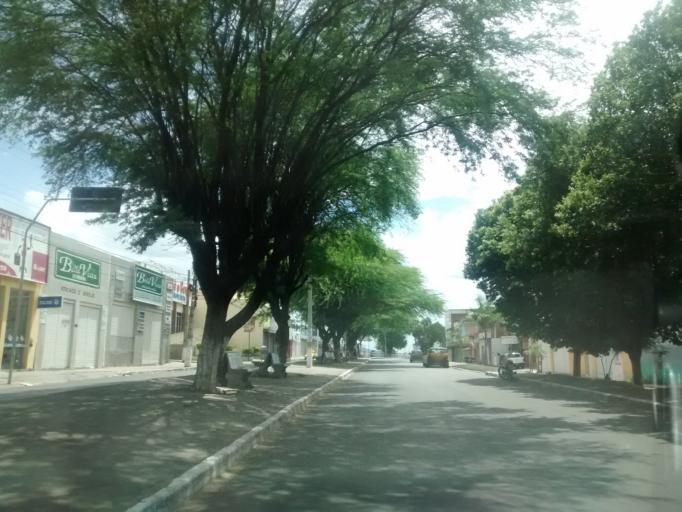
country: BR
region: Bahia
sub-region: Brumado
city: Brumado
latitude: -14.2118
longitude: -41.6736
